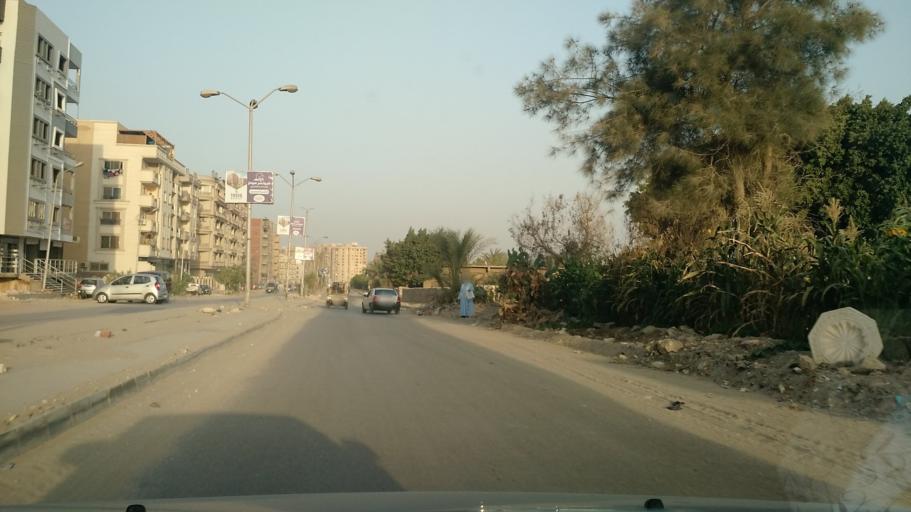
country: EG
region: Muhafazat al Qahirah
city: Cairo
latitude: 29.9948
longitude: 31.2941
